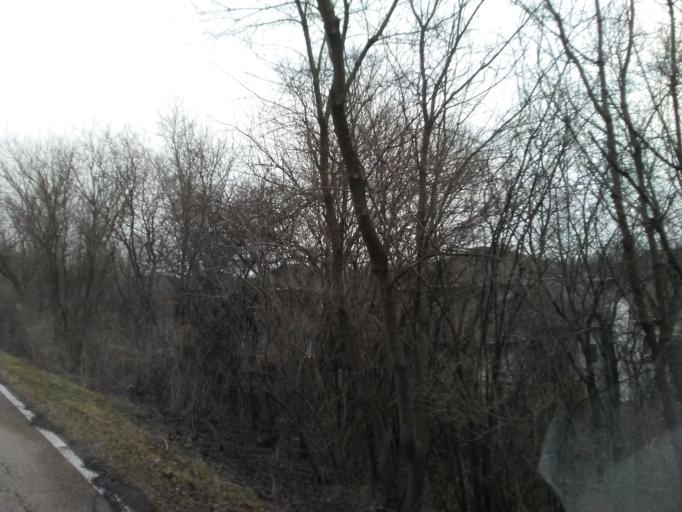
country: US
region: Wisconsin
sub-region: Dane County
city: Middleton
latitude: 43.1091
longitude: -89.4937
